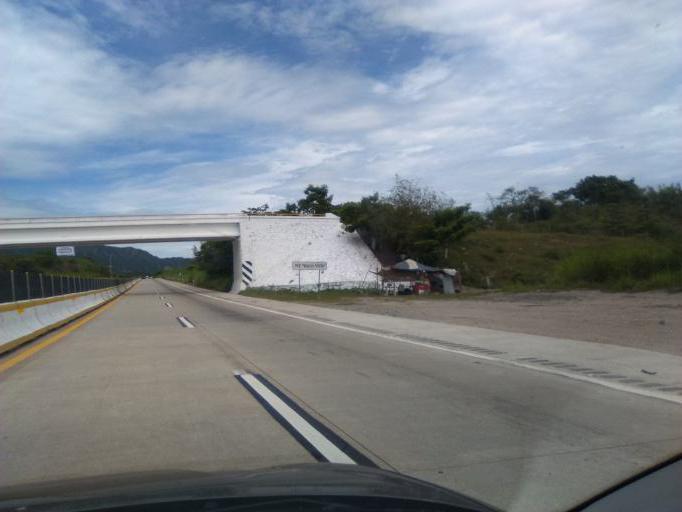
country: MX
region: Guerrero
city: El Ocotito
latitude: 17.2641
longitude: -99.5138
